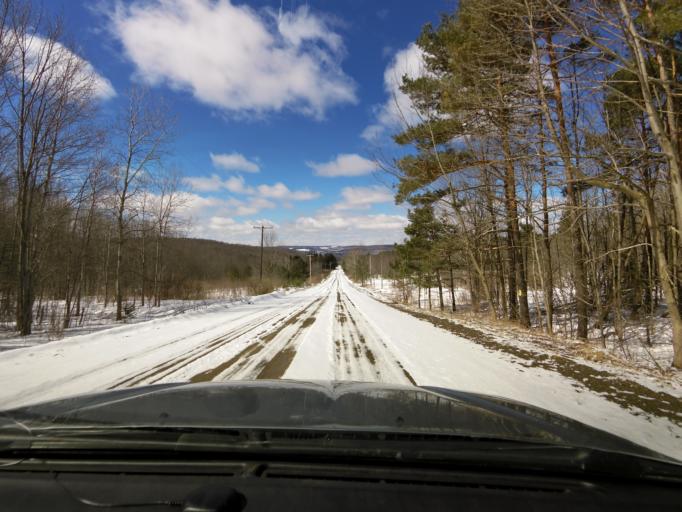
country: US
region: New York
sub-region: Cattaraugus County
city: Franklinville
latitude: 42.3429
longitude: -78.3986
